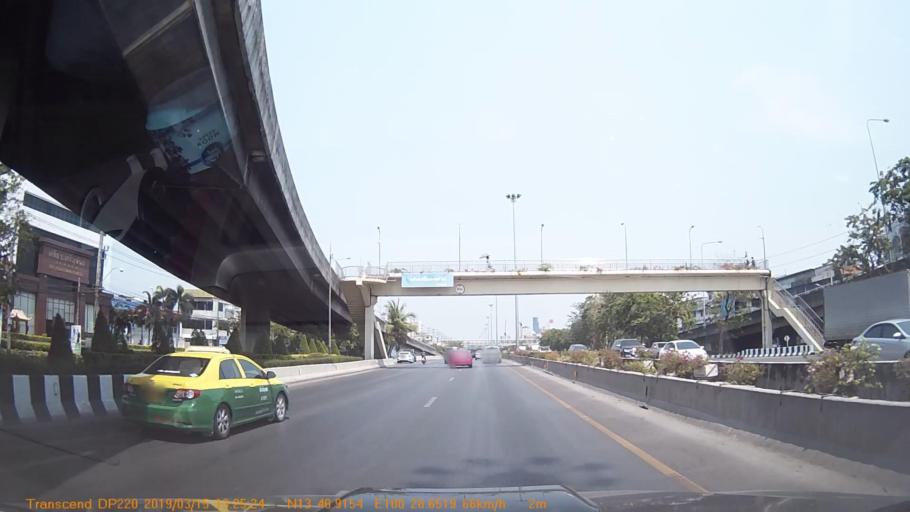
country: TH
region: Bangkok
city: Chom Thong
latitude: 13.6820
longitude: 100.4779
